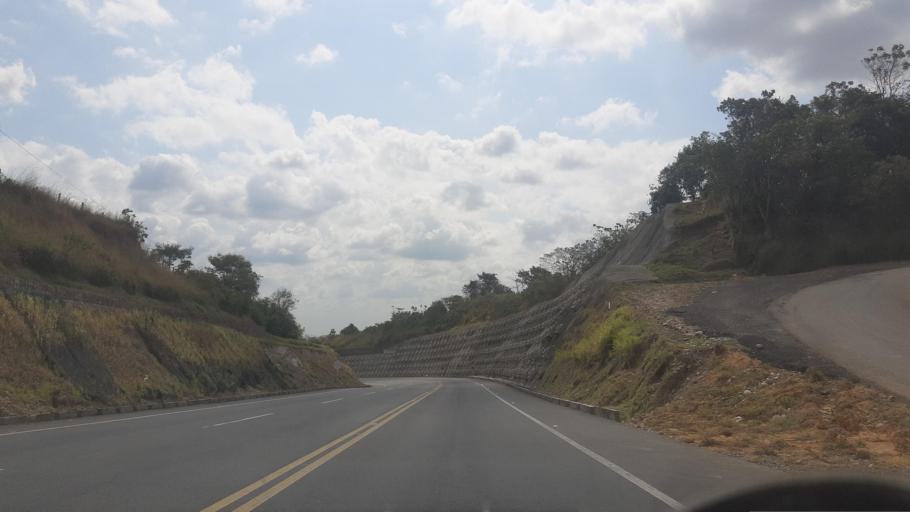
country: CO
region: Casanare
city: Monterrey
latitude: 4.8342
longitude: -72.8244
